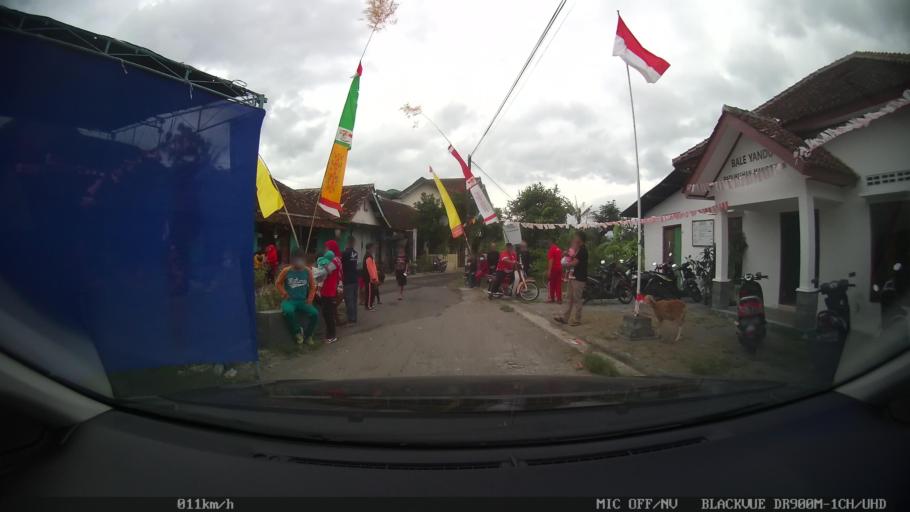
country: ID
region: Daerah Istimewa Yogyakarta
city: Sewon
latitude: -7.8327
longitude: 110.4083
